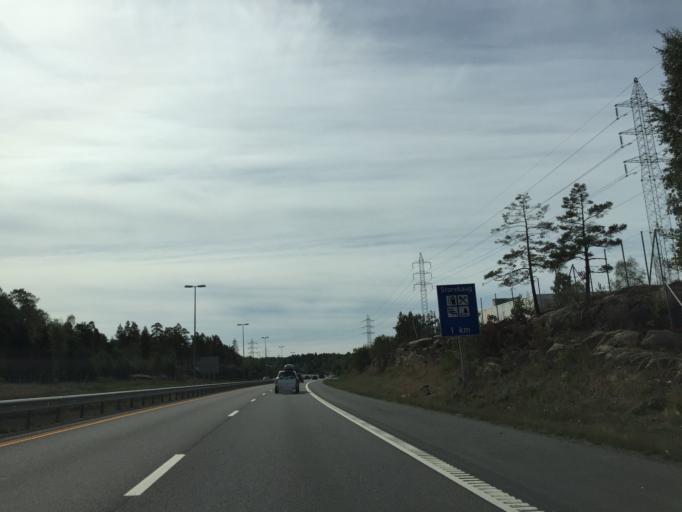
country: NO
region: Ostfold
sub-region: Moss
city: Moss
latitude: 59.4384
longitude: 10.7062
